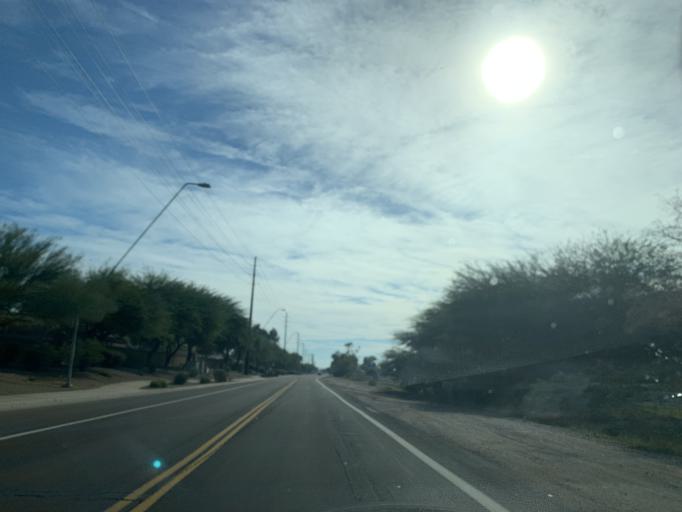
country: US
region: Arizona
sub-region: Maricopa County
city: Sun Lakes
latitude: 33.2291
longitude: -111.8066
